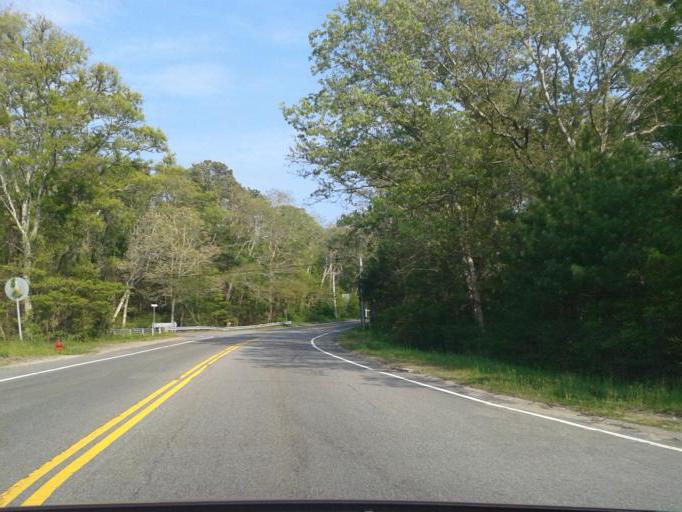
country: US
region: Massachusetts
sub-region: Barnstable County
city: West Falmouth
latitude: 41.5942
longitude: -70.6268
